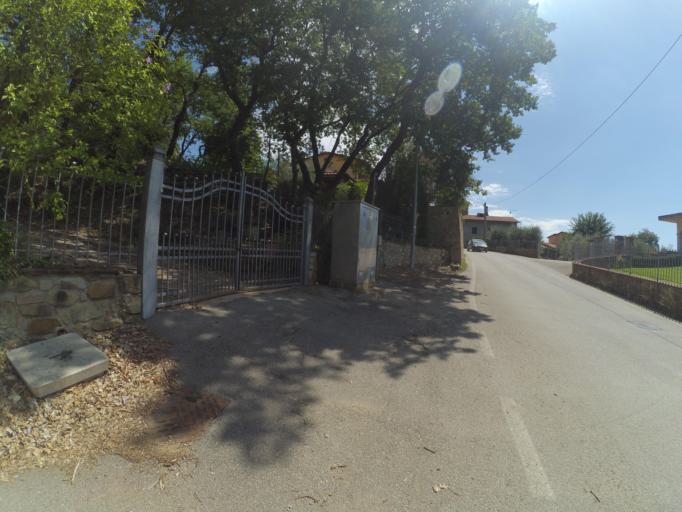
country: IT
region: Tuscany
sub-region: Province of Arezzo
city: Castiglion Fibocchi
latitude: 43.5301
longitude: 11.7713
